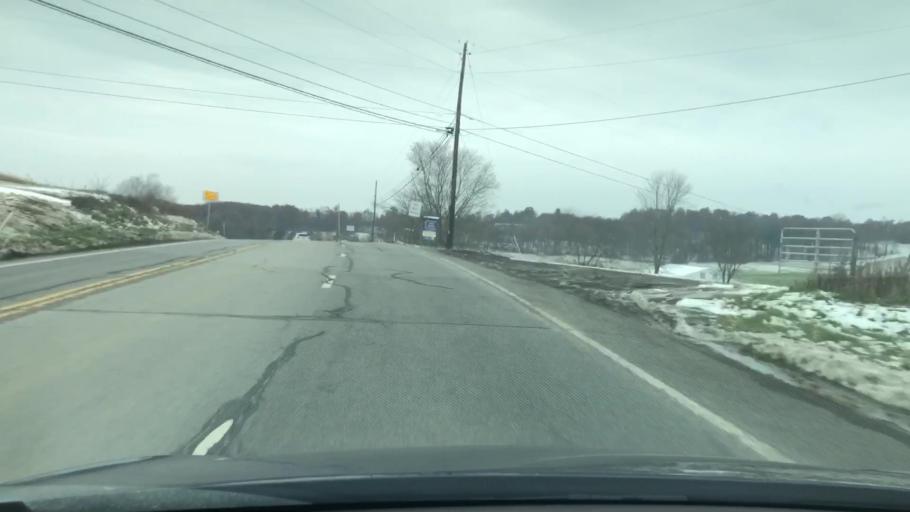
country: US
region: Pennsylvania
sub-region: Jefferson County
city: Brookville
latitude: 41.1111
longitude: -79.2102
